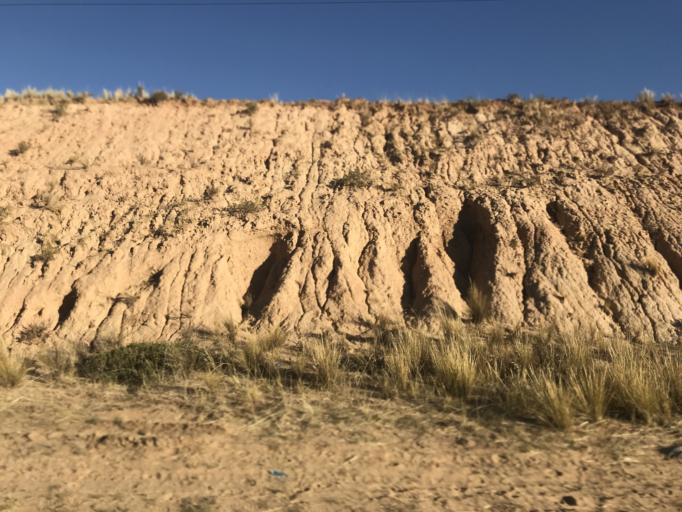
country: BO
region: La Paz
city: Tiahuanaco
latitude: -16.5640
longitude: -68.6327
